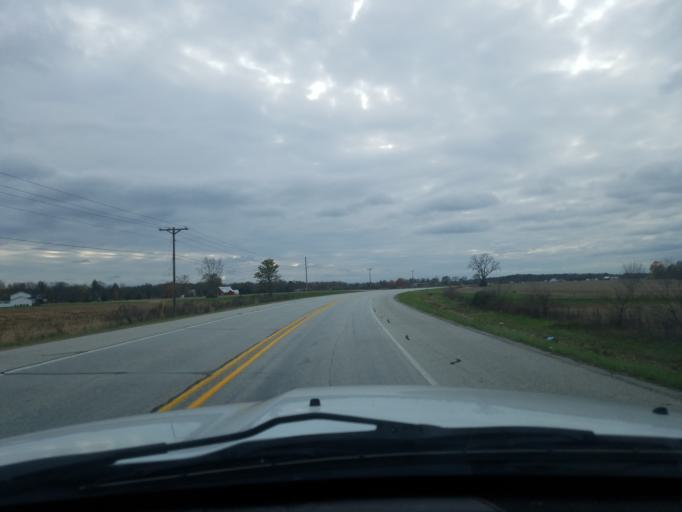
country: US
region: Indiana
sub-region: Bartholomew County
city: Hope
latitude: 39.1805
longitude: -85.7735
